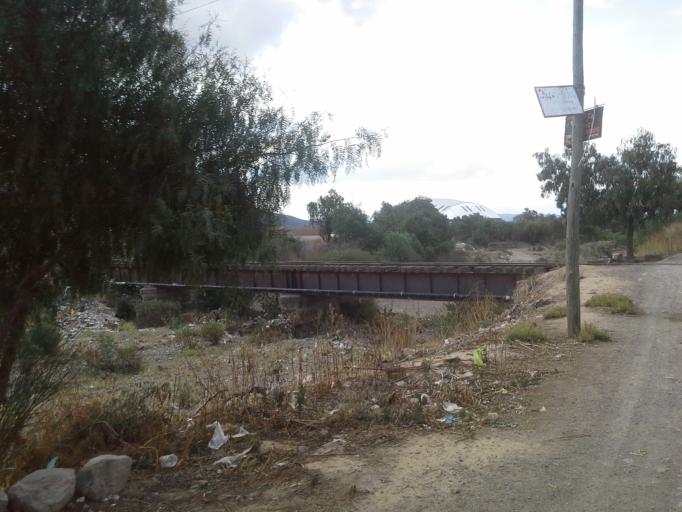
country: BO
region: Cochabamba
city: Tarata
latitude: -17.6082
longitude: -66.0212
